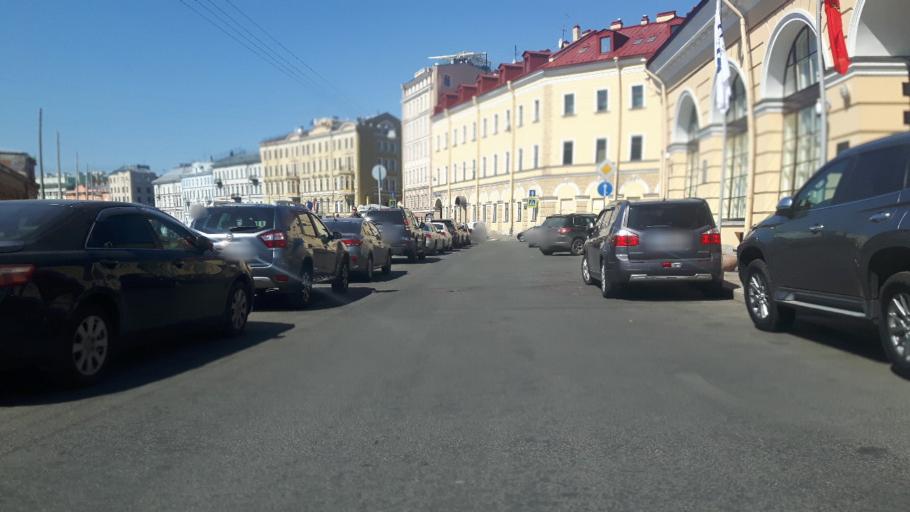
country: RU
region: St.-Petersburg
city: Saint Petersburg
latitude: 59.9422
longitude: 30.3275
